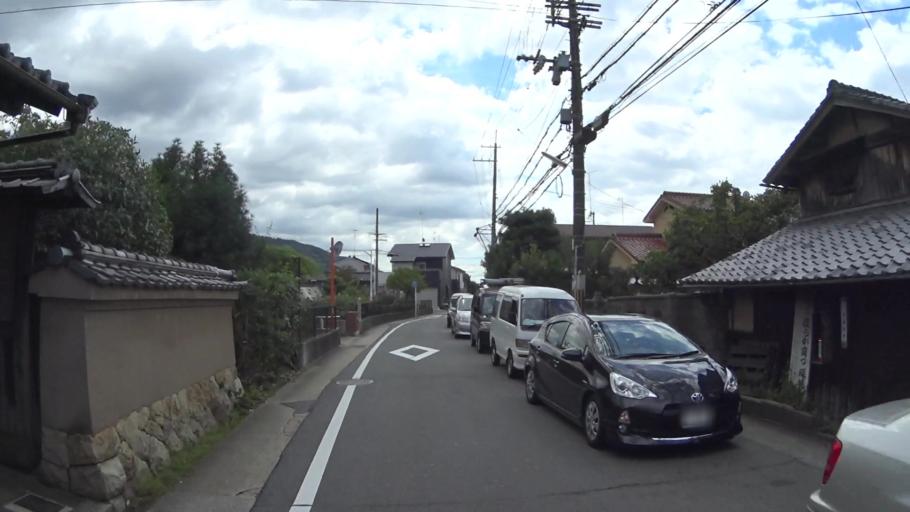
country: JP
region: Shiga Prefecture
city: Otsu-shi
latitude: 34.9788
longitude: 135.8239
